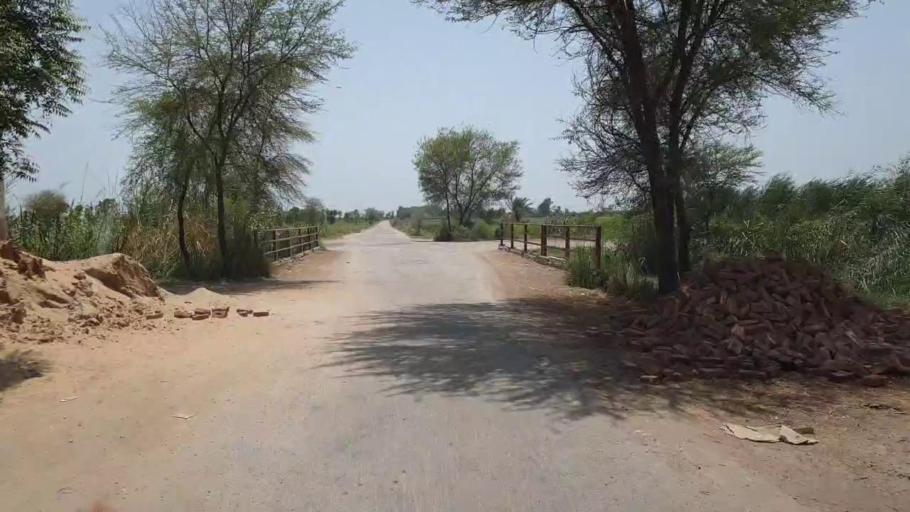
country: PK
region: Sindh
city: Daur
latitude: 26.3916
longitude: 68.1986
